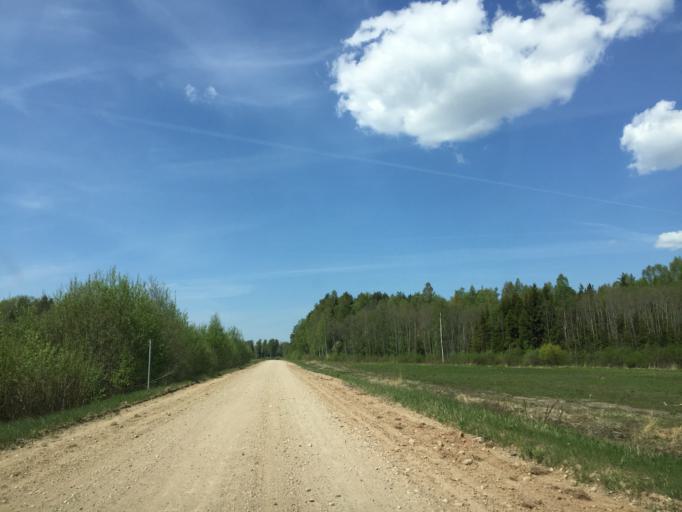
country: LV
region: Limbazu Rajons
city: Limbazi
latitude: 57.3854
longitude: 24.5816
